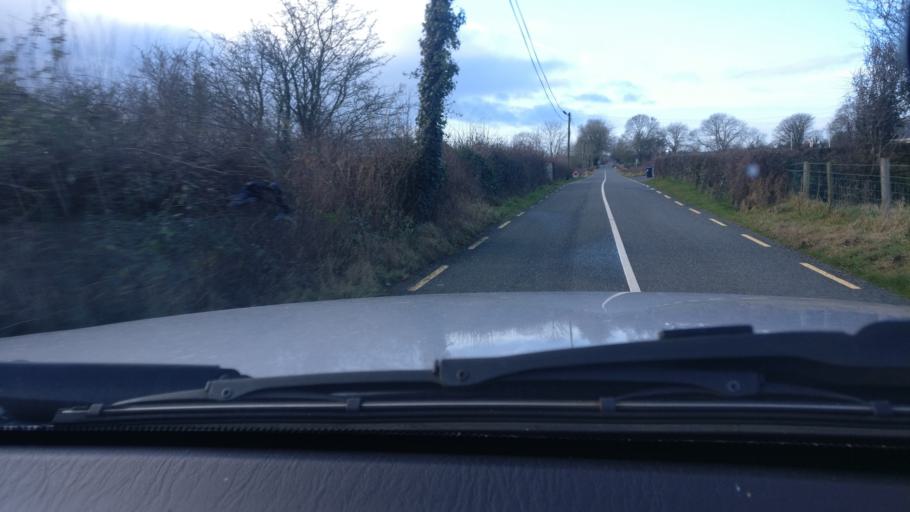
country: IE
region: Connaught
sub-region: County Galway
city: Ballinasloe
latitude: 53.2293
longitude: -8.3097
